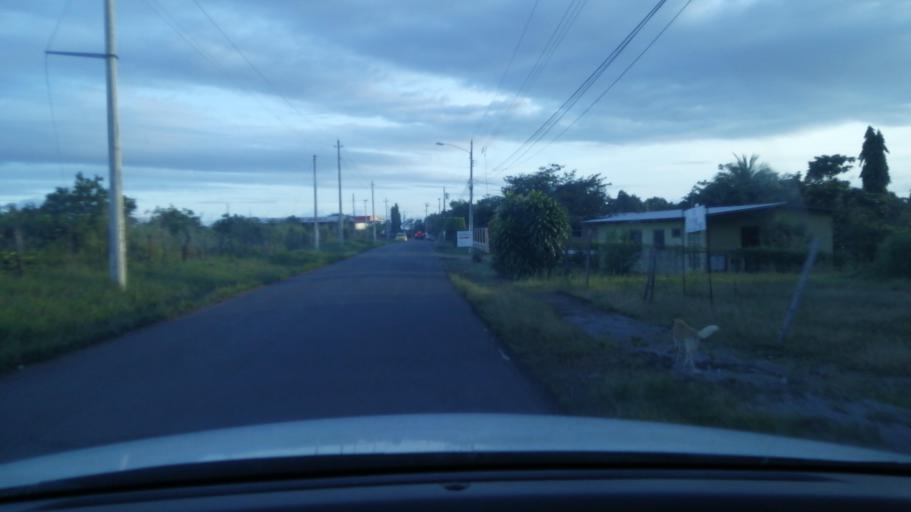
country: PA
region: Chiriqui
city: David
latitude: 8.4036
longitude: -82.4355
